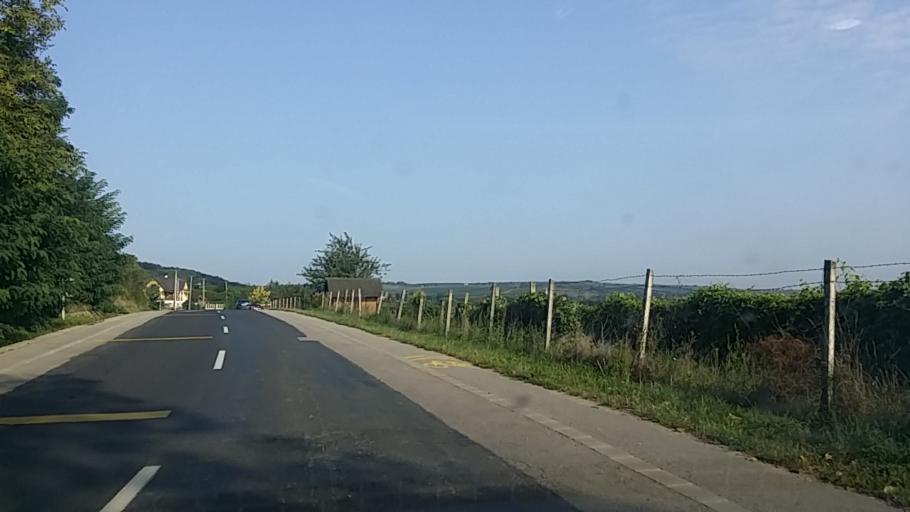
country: HU
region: Gyor-Moson-Sopron
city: Nagycenk
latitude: 47.6412
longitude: 16.6747
